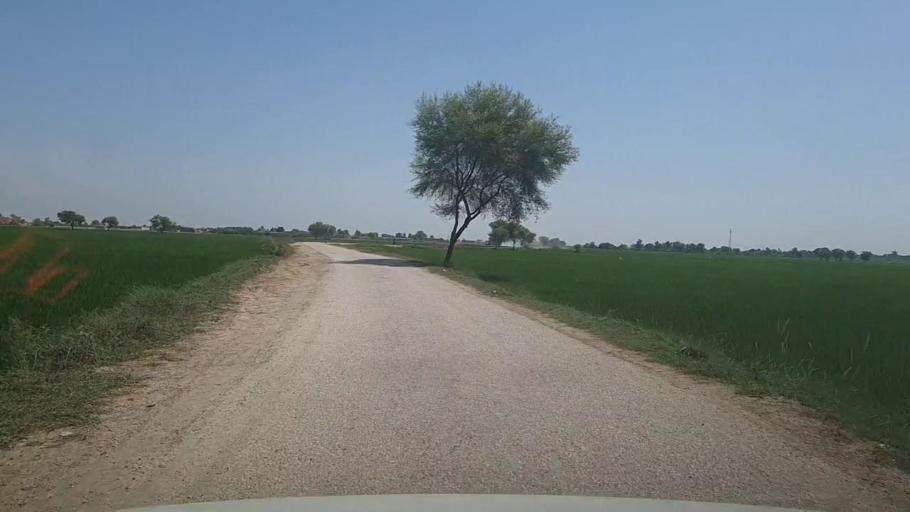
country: PK
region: Sindh
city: Kashmor
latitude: 28.2951
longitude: 69.4337
